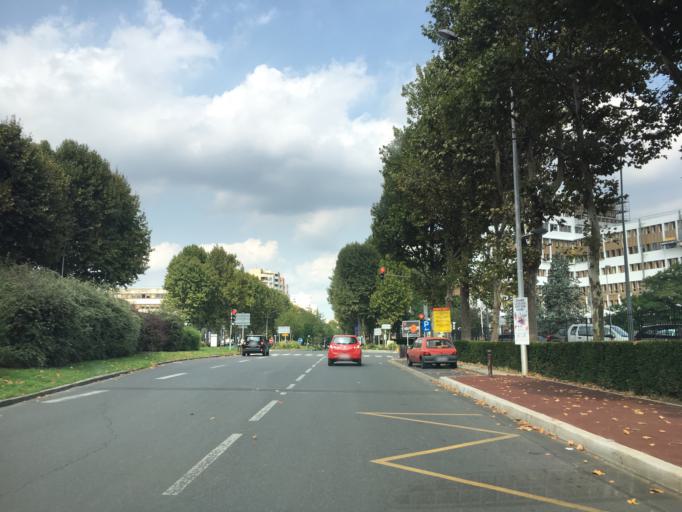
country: FR
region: Ile-de-France
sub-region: Departement du Val-de-Marne
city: Maisons-Alfort
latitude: 48.7934
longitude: 2.4469
